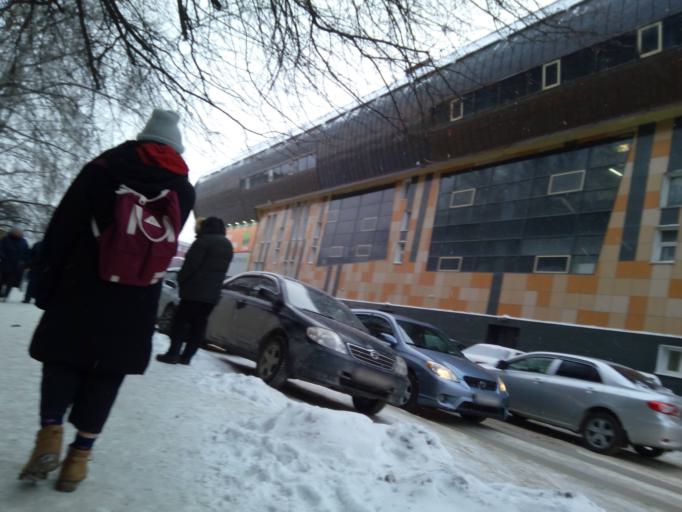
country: RU
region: Novosibirsk
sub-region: Novosibirskiy Rayon
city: Novosibirsk
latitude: 54.9894
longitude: 82.9049
